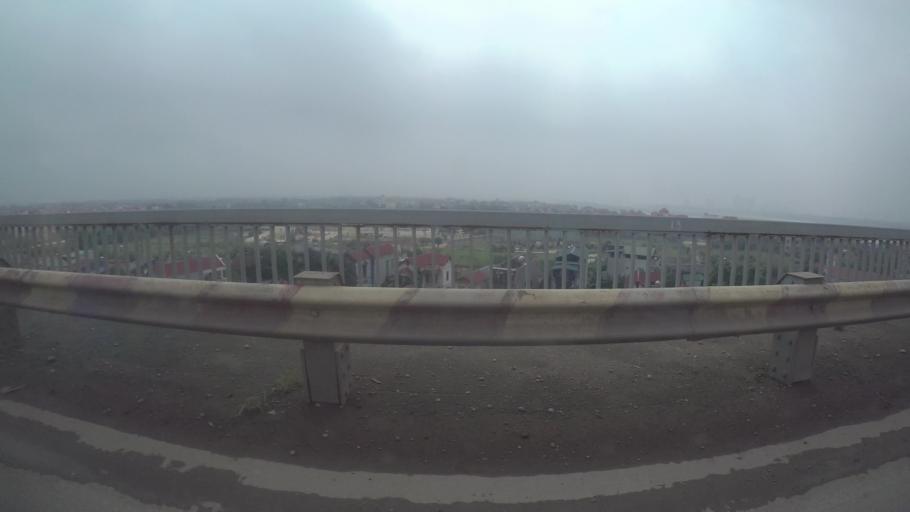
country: VN
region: Ha Noi
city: Tay Ho
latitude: 21.1050
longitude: 105.7870
